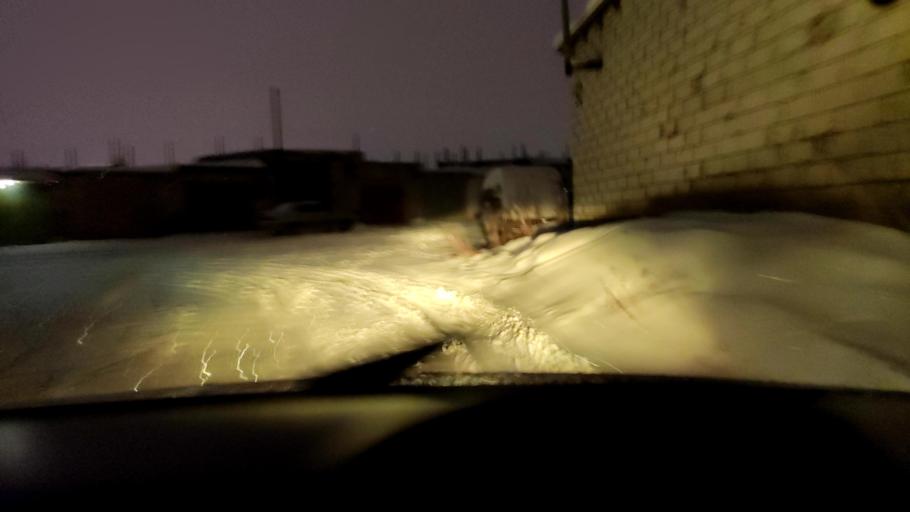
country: RU
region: Voronezj
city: Pridonskoy
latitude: 51.6360
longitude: 39.1236
